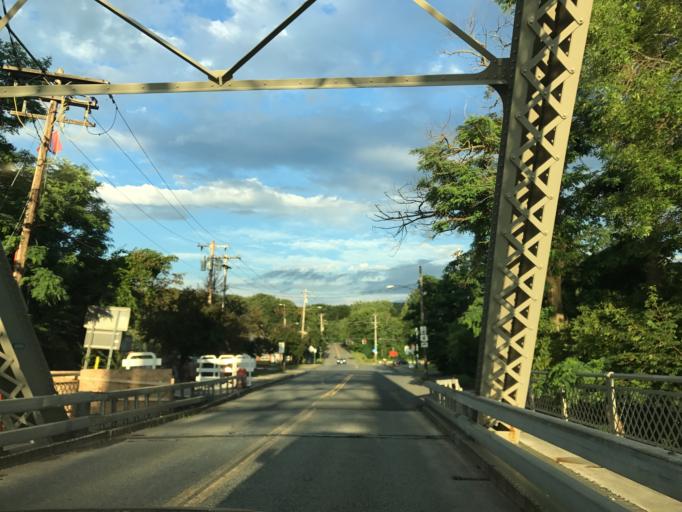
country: US
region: New York
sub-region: Saratoga County
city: Waterford
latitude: 42.7883
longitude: -73.6729
